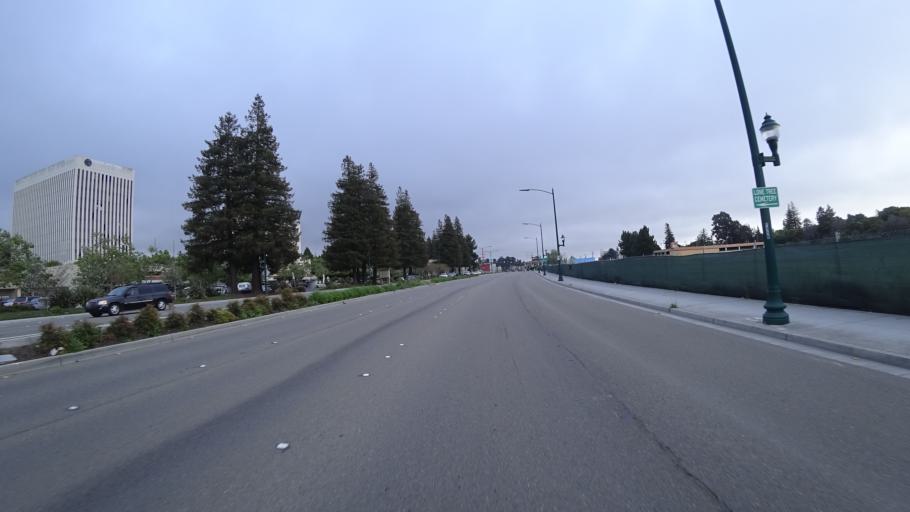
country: US
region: California
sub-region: Alameda County
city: Hayward
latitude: 37.6793
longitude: -122.0847
